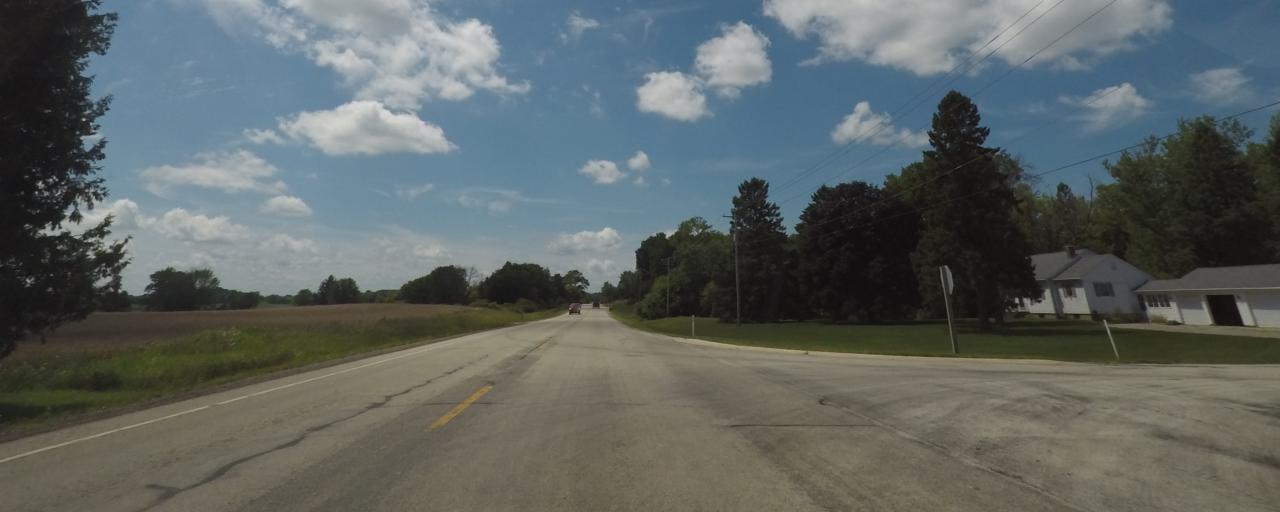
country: US
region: Wisconsin
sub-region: Jefferson County
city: Fort Atkinson
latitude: 42.9390
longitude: -88.7633
